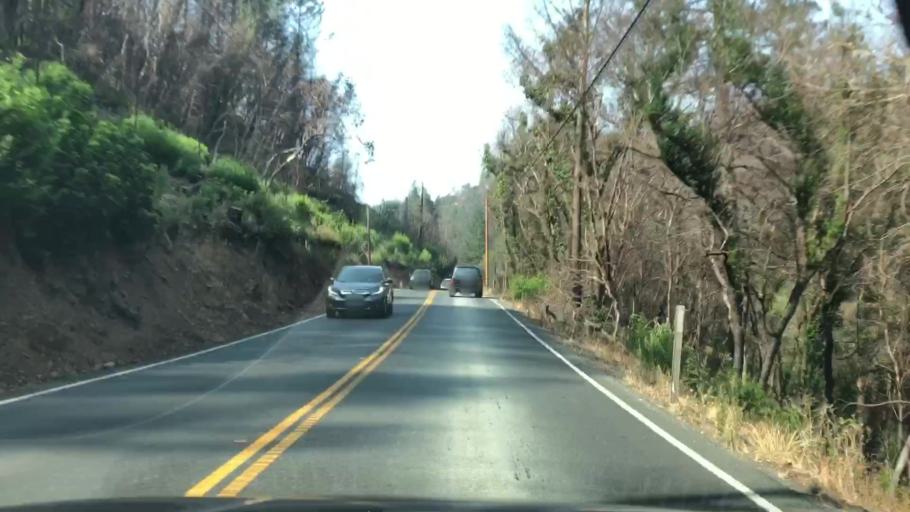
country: US
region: California
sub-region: Sonoma County
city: Larkfield-Wikiup
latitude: 38.5383
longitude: -122.7226
